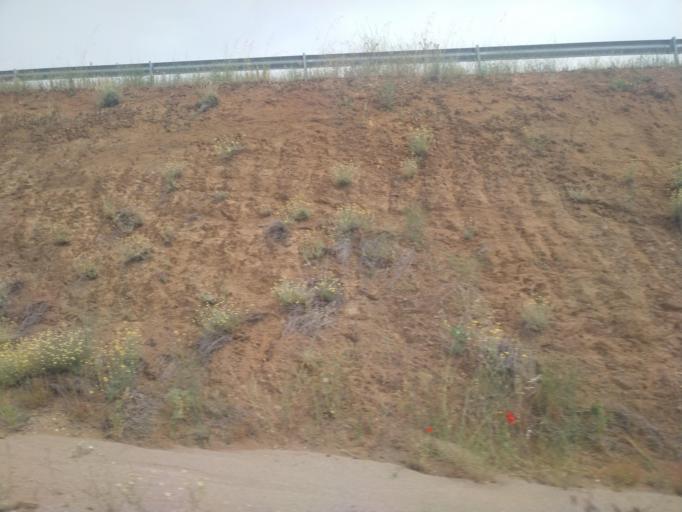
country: ES
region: Castille-La Mancha
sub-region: Province of Toledo
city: Polan
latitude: 39.7878
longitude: -4.1552
